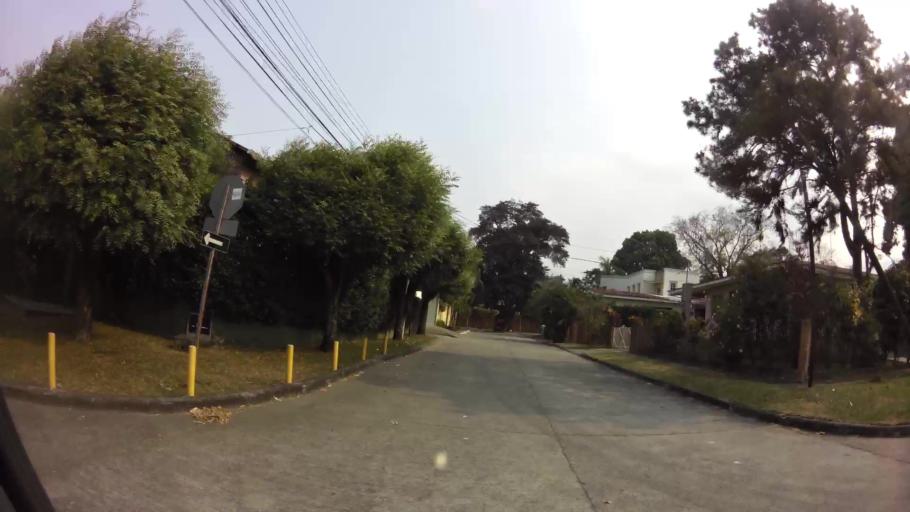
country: HN
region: Cortes
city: El Zapotal del Norte
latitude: 15.5109
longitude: -88.0428
